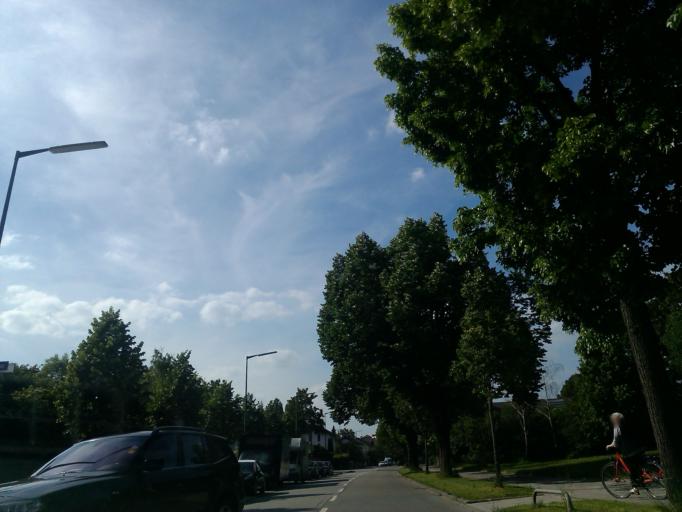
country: DE
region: Bavaria
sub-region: Upper Bavaria
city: Pasing
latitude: 48.1613
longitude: 11.4451
